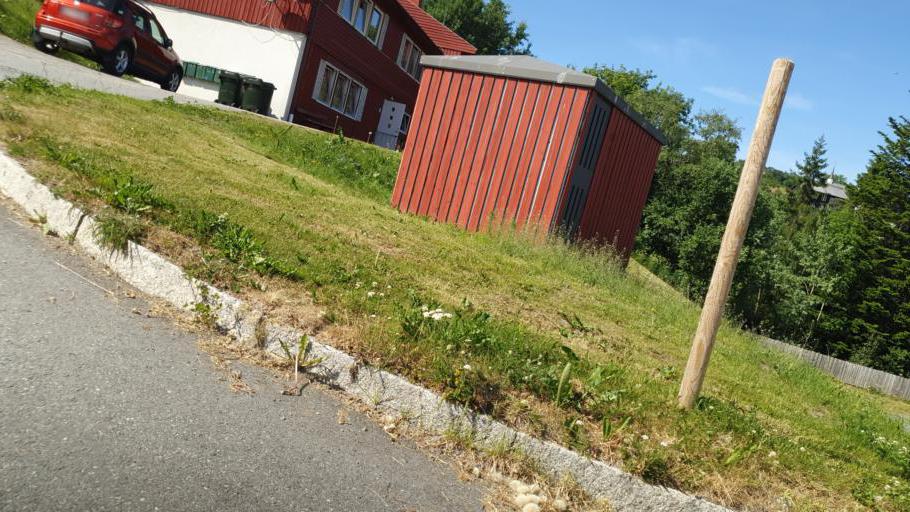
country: NO
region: Nord-Trondelag
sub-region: Leksvik
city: Leksvik
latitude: 63.6728
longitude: 10.6296
